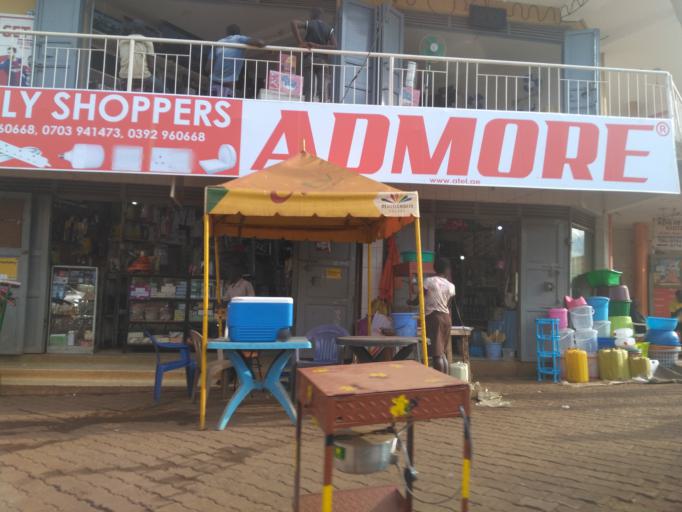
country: UG
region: Eastern Region
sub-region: Jinja District
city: Jinja
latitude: 0.4305
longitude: 33.2113
